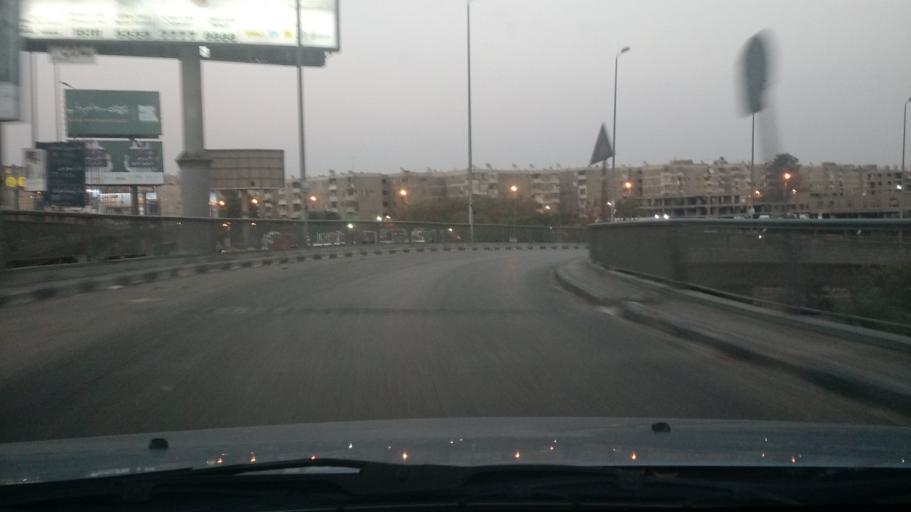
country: EG
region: Al Jizah
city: Al Jizah
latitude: 29.9918
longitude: 31.2844
